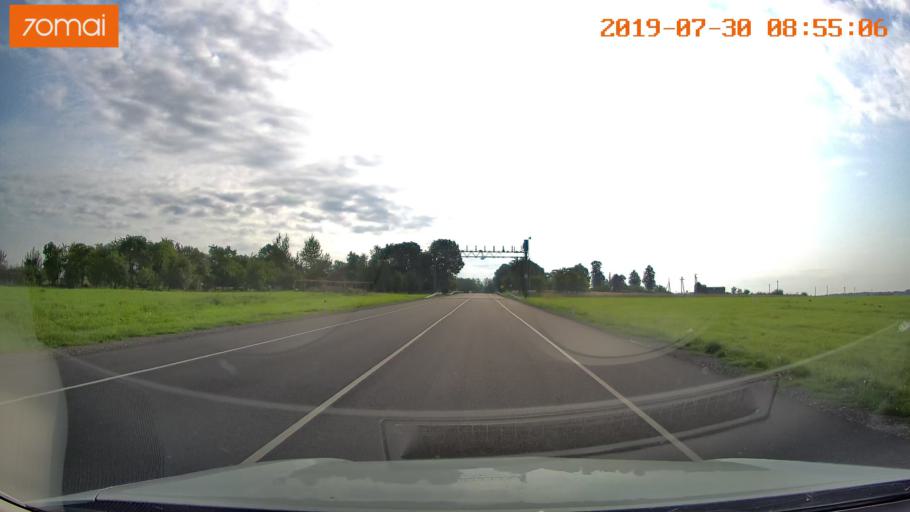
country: RU
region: Kaliningrad
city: Gusev
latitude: 54.6018
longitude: 22.0422
